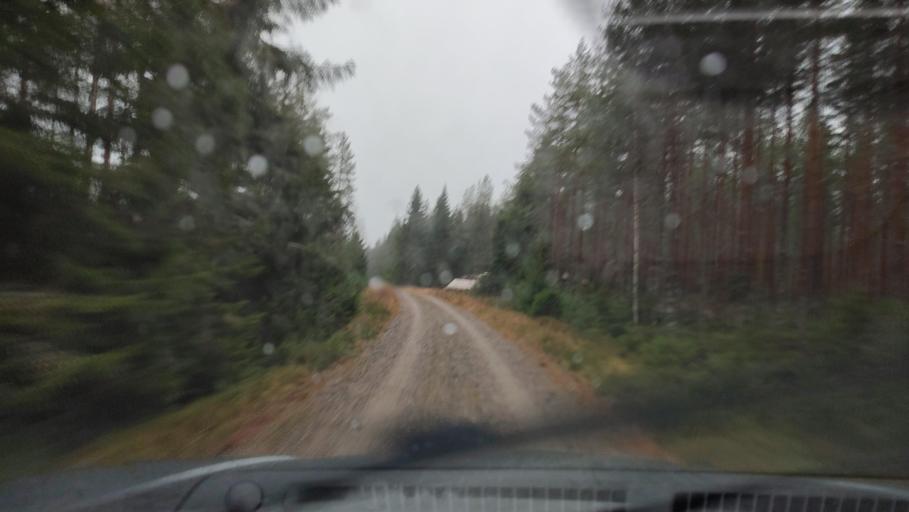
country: FI
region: Southern Ostrobothnia
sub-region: Suupohja
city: Karijoki
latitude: 62.1822
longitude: 21.7323
